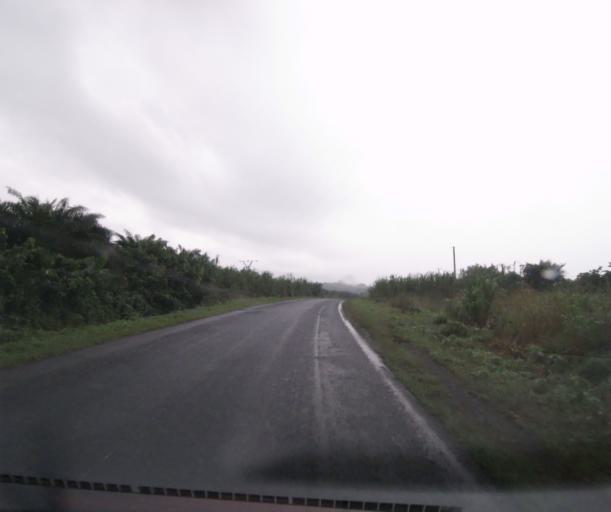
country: CM
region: South-West Province
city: Idenao
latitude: 4.1803
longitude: 9.0027
